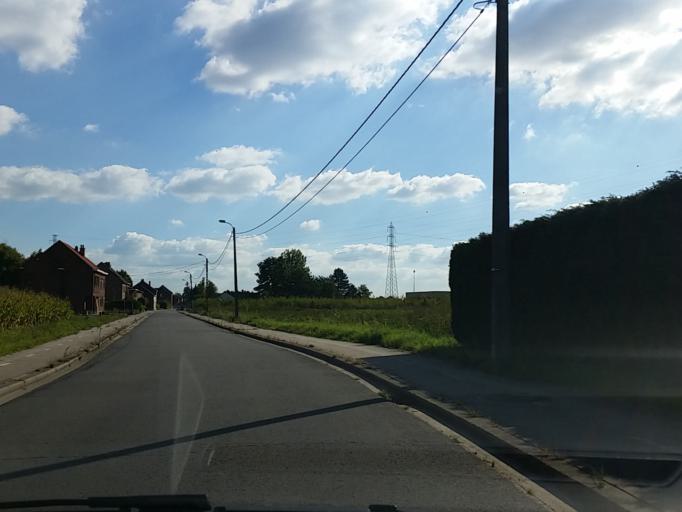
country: BE
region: Flanders
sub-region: Provincie Vlaams-Brabant
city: Rotselaar
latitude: 50.9410
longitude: 4.6933
